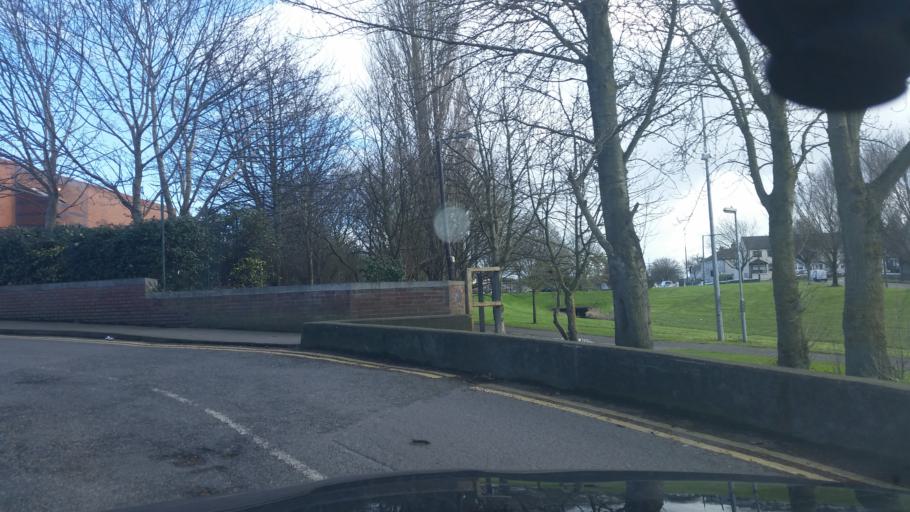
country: IE
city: Coolock
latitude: 53.3910
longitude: -6.1941
